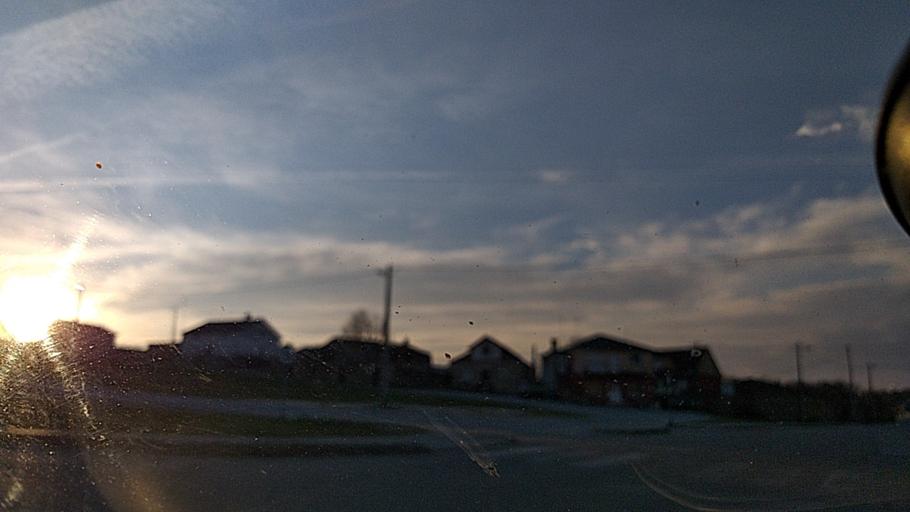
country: PT
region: Guarda
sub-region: Guarda
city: Sequeira
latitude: 40.6013
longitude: -7.0688
